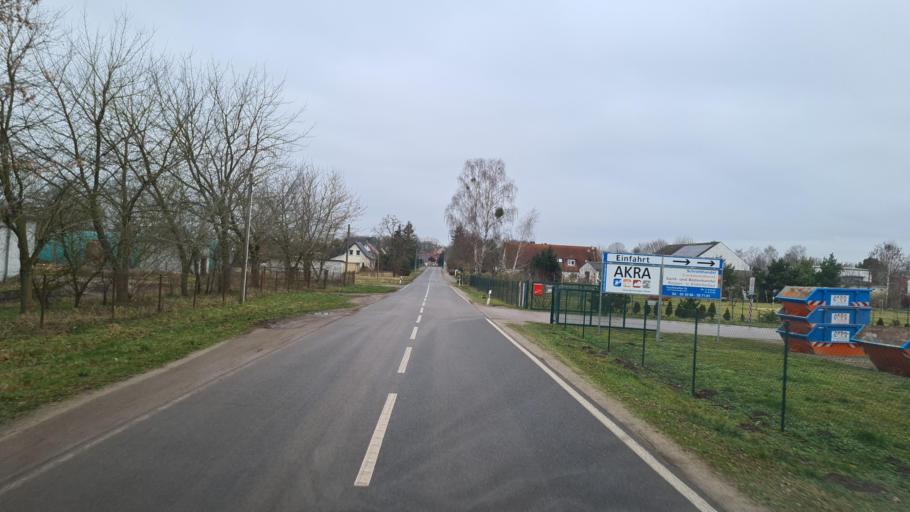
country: DE
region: Brandenburg
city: Gransee
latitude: 52.9417
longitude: 13.2208
